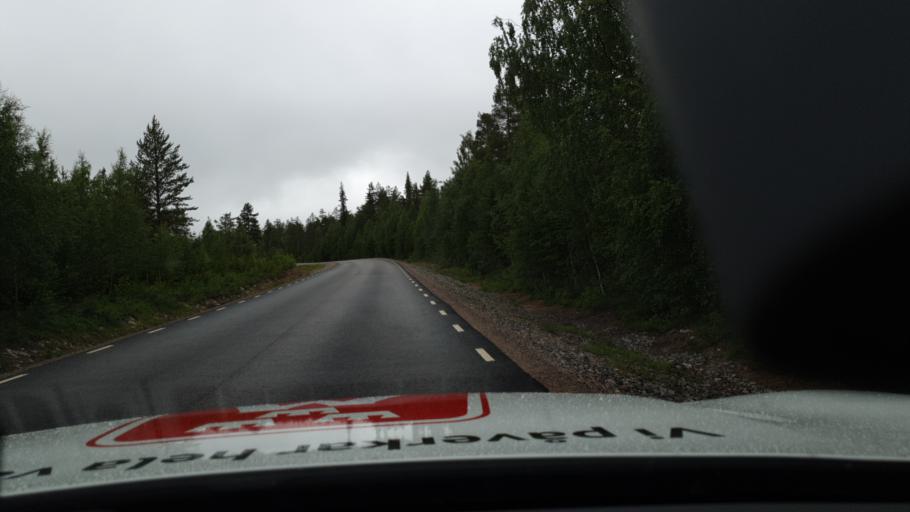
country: SE
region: Norrbotten
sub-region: Overtornea Kommun
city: OEvertornea
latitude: 66.4366
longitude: 23.5090
